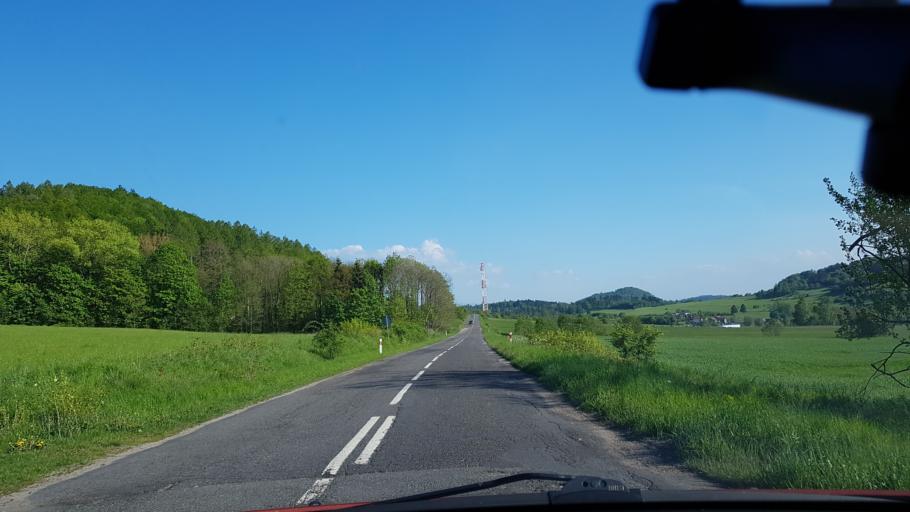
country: PL
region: Lower Silesian Voivodeship
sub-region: Powiat klodzki
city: Bozkow
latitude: 50.5857
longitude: 16.5831
